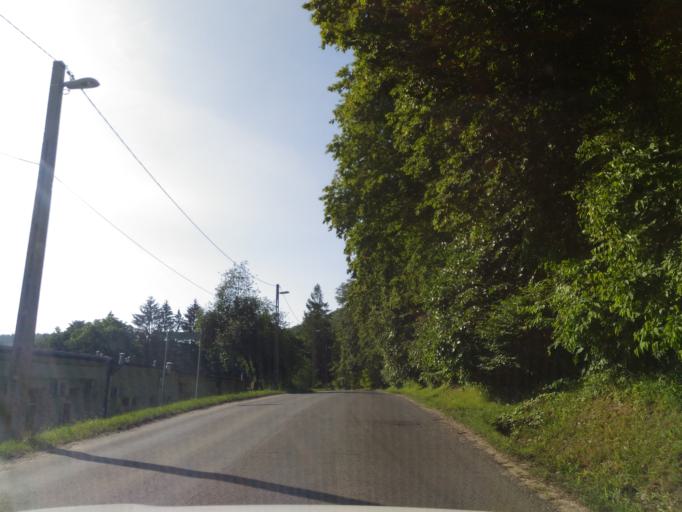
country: HU
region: Baranya
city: Komlo
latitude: 46.1858
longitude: 18.2843
